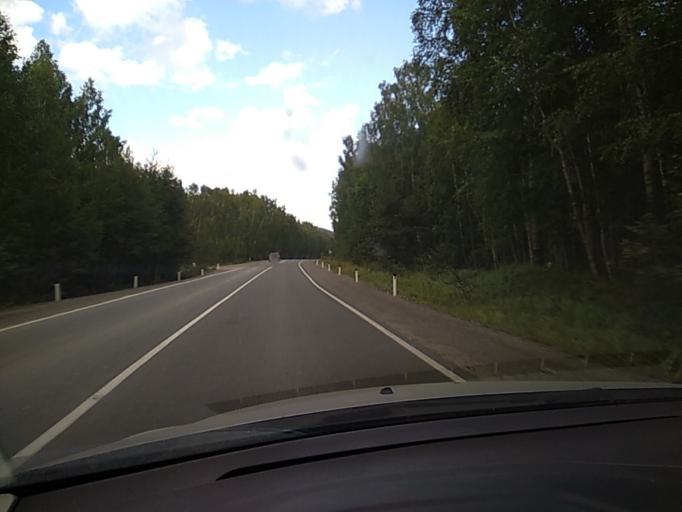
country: RU
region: Chelyabinsk
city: Karabash
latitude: 55.4995
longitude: 60.2572
